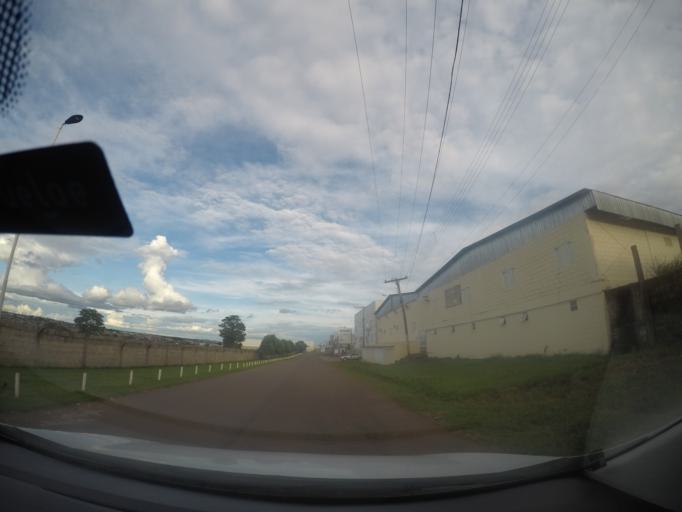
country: BR
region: Goias
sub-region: Goiania
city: Goiania
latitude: -16.6233
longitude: -49.3507
